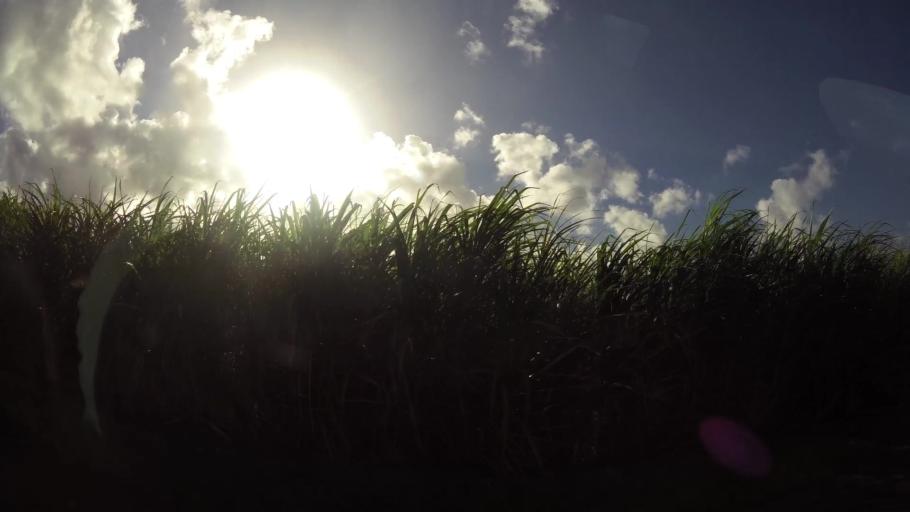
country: MQ
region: Martinique
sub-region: Martinique
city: Ducos
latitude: 14.5991
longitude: -60.9752
